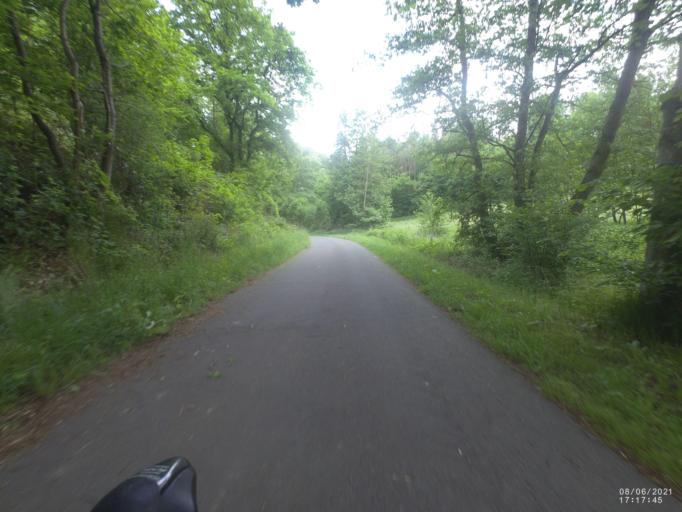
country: DE
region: Rheinland-Pfalz
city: Kalt
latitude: 50.2479
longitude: 7.3977
